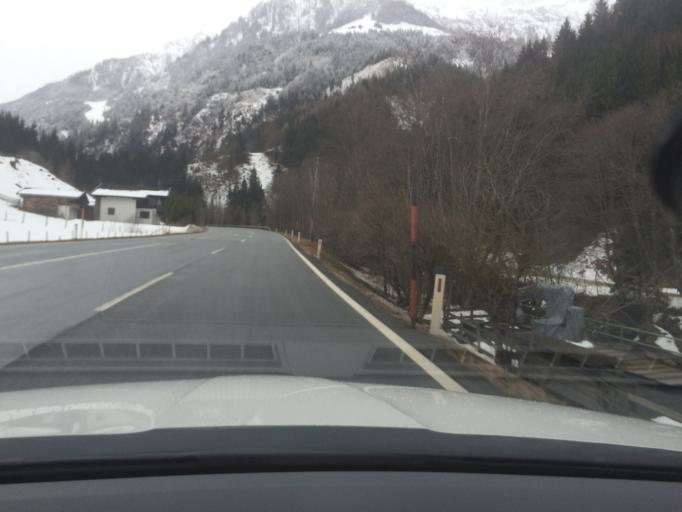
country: AT
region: Salzburg
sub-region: Politischer Bezirk Zell am See
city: Mittersill
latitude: 47.2598
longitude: 12.4841
